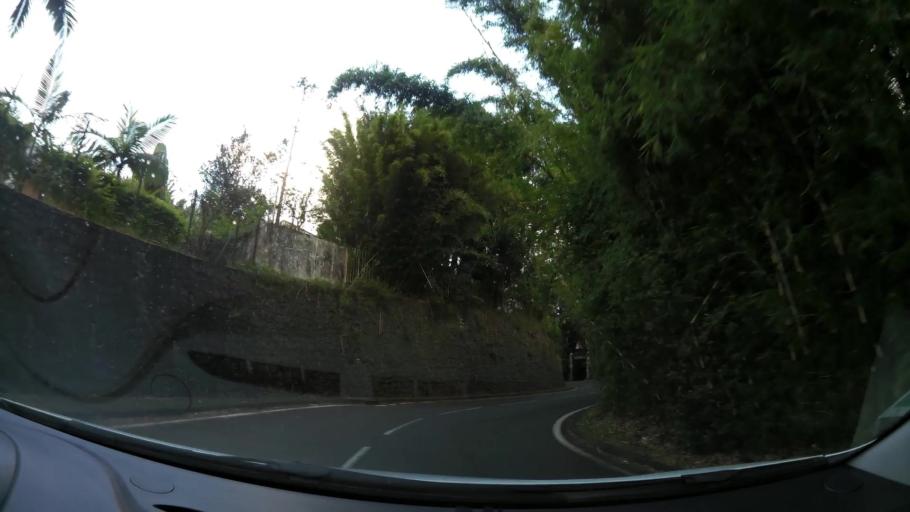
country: RE
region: Reunion
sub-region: Reunion
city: Saint-Denis
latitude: -20.9215
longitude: 55.4349
